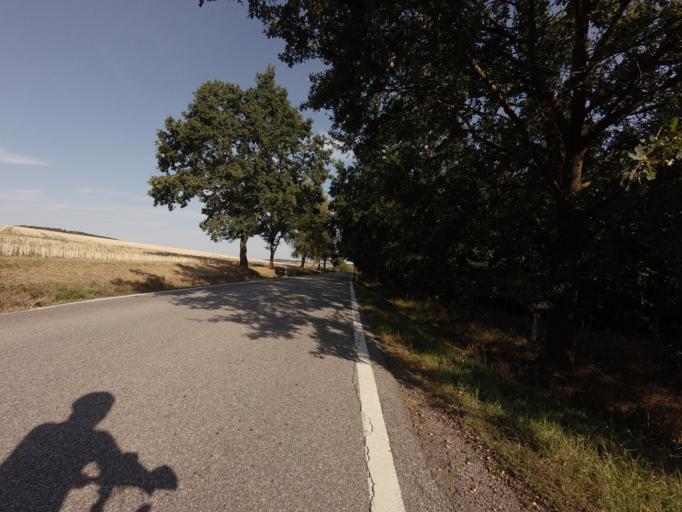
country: CZ
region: Jihocesky
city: Tyn nad Vltavou
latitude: 49.2703
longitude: 14.4072
